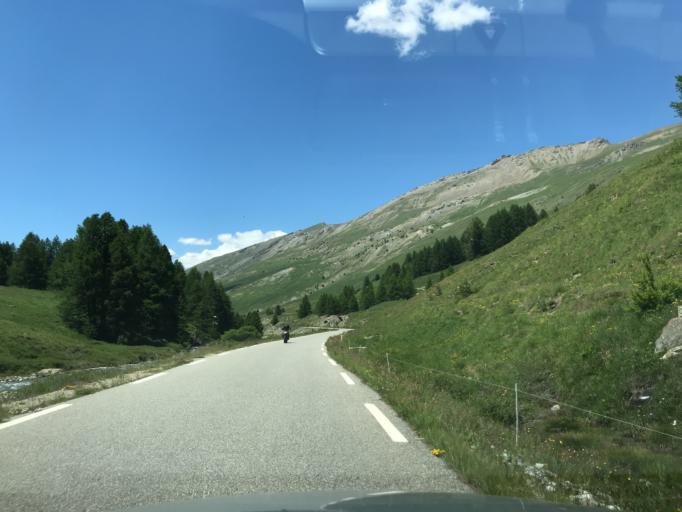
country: IT
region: Piedmont
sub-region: Provincia di Cuneo
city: Pontechianale
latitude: 44.7136
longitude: 6.9180
